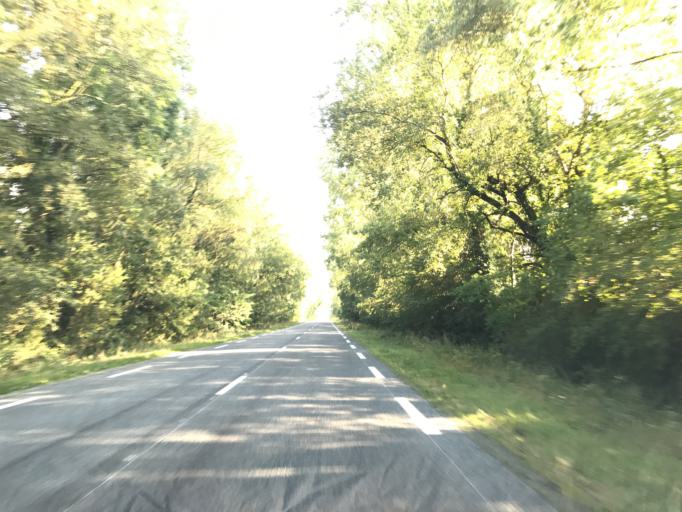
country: FR
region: Haute-Normandie
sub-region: Departement de la Seine-Maritime
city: La Cerlangue
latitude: 49.5213
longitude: 0.4196
